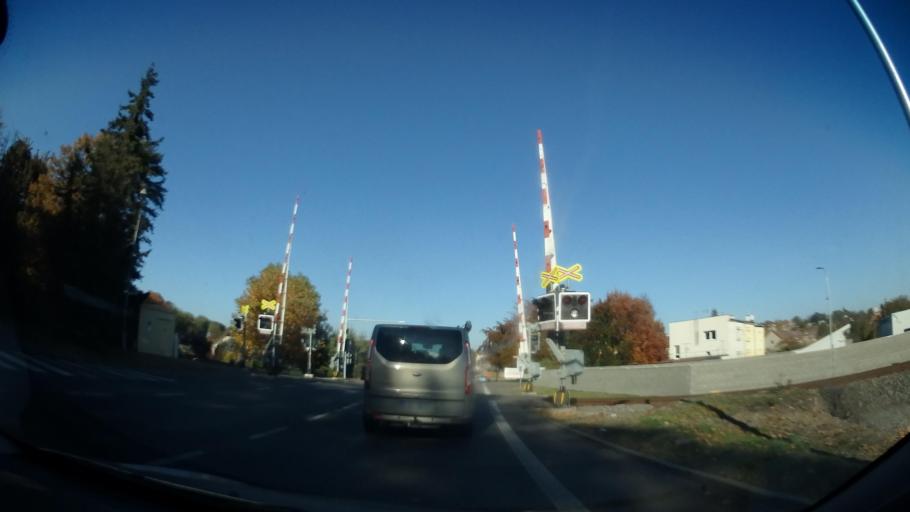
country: CZ
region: Pardubicky
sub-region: Okres Chrudim
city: Chrudim
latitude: 49.9399
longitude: 15.7945
